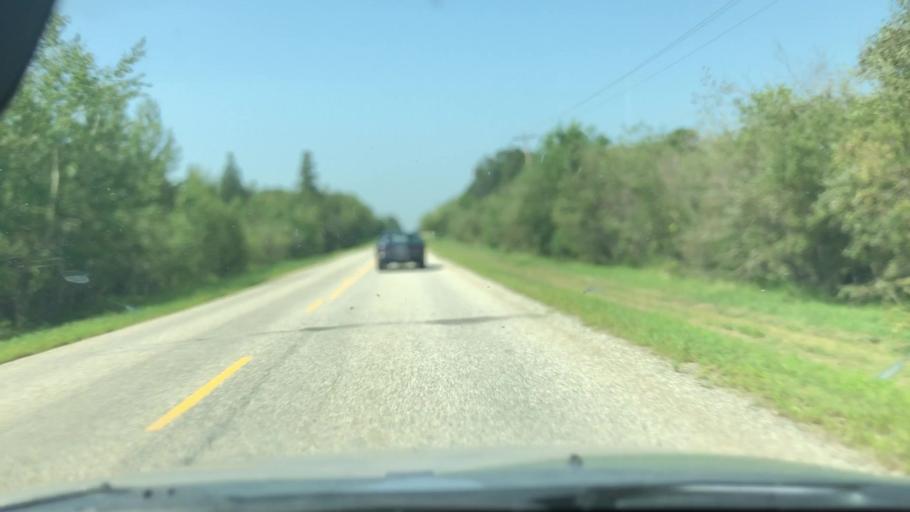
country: CA
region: Alberta
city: Devon
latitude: 53.4252
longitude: -113.7798
